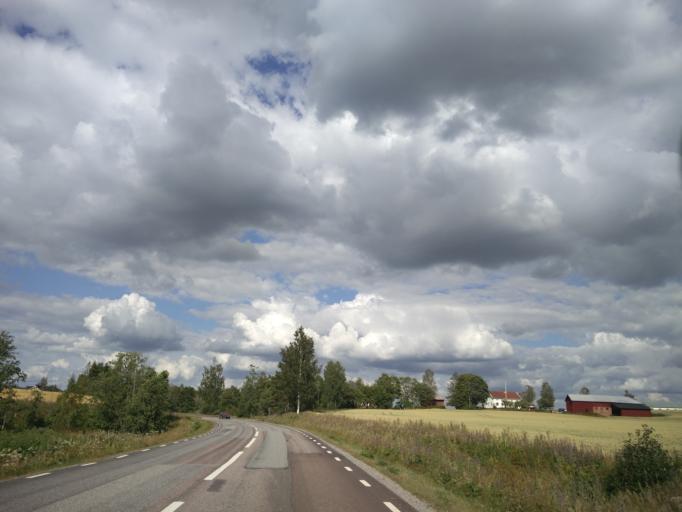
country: SE
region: Vaermland
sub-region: Sunne Kommun
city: Sunne
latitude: 59.7221
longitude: 13.1163
